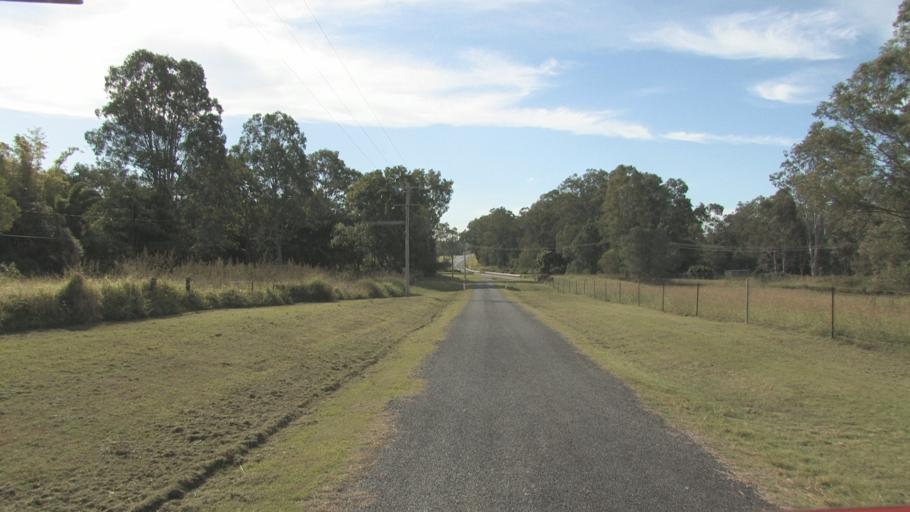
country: AU
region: Queensland
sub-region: Logan
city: Windaroo
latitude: -27.7632
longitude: 153.1852
